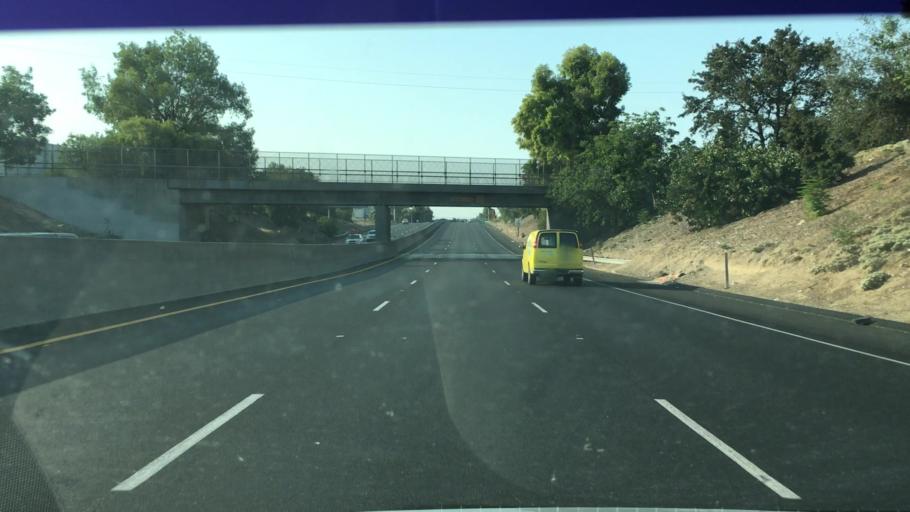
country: US
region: California
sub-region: San Joaquin County
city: August
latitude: 37.9766
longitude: -121.2487
